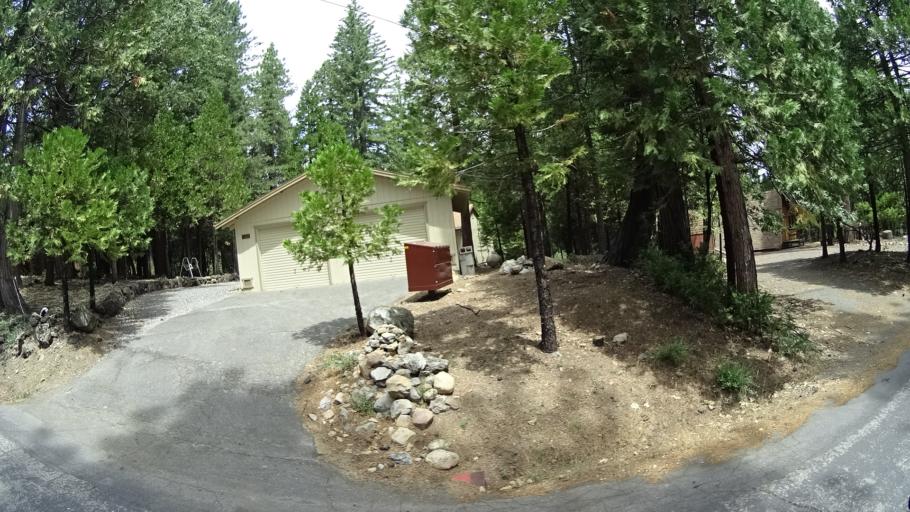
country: US
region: California
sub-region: Calaveras County
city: Arnold
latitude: 38.2511
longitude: -120.3455
